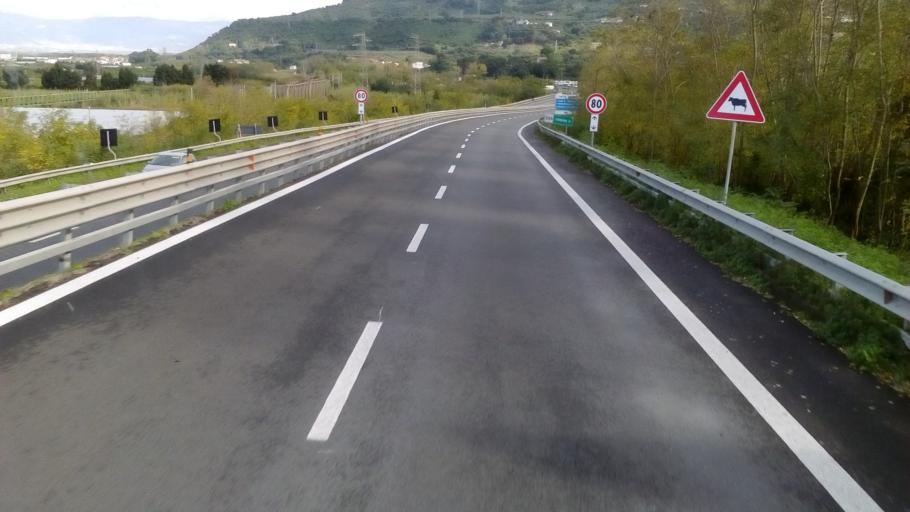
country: IT
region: Calabria
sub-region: Provincia di Vibo-Valentia
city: Pizzo
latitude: 38.7689
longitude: 16.2084
